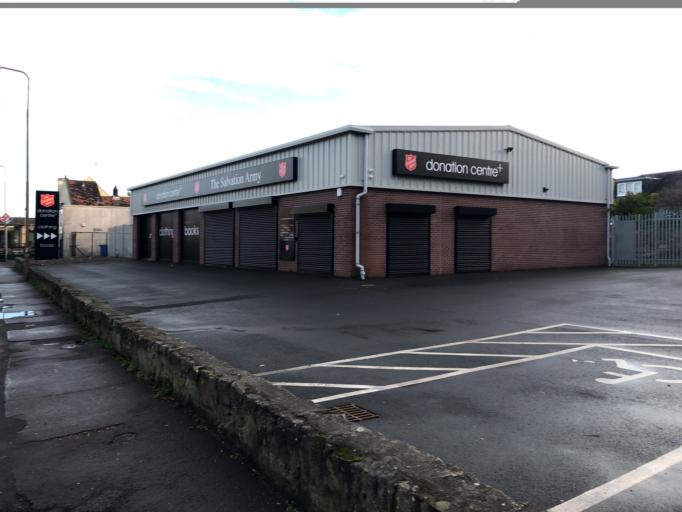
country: GB
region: Scotland
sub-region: West Lothian
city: Seafield
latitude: 55.9551
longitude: -3.1456
